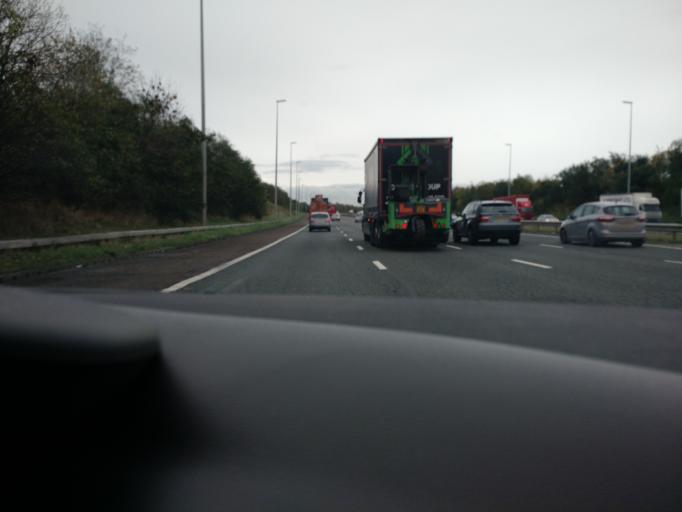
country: GB
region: England
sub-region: Lancashire
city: Goosnargh
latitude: 53.7939
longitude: -2.6726
